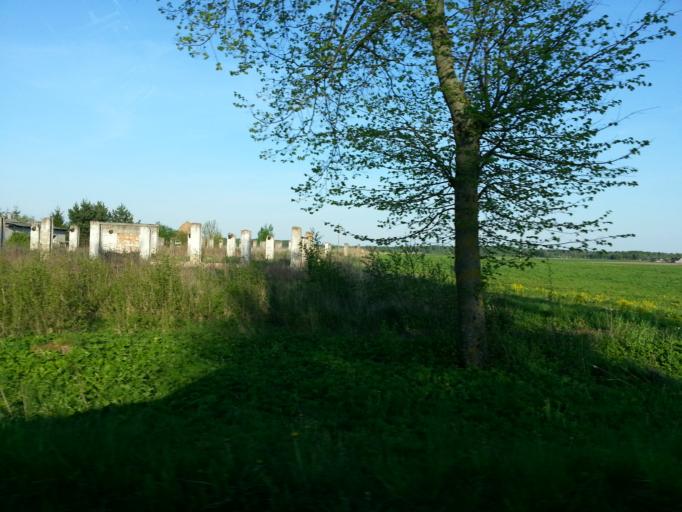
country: LT
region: Vilnius County
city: Ukmerge
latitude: 55.4215
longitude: 24.5845
